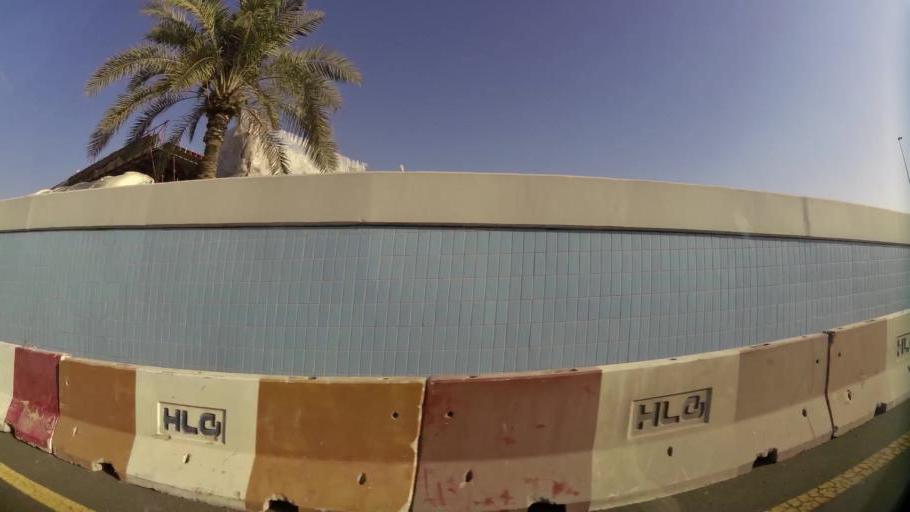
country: AE
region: Ash Shariqah
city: Sharjah
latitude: 25.2381
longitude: 55.3761
